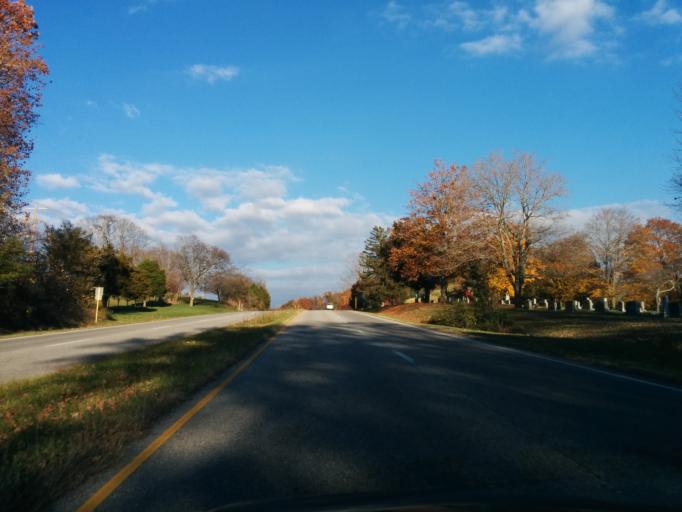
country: US
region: Virginia
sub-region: Rockbridge County
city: East Lexington
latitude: 37.8441
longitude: -79.3572
